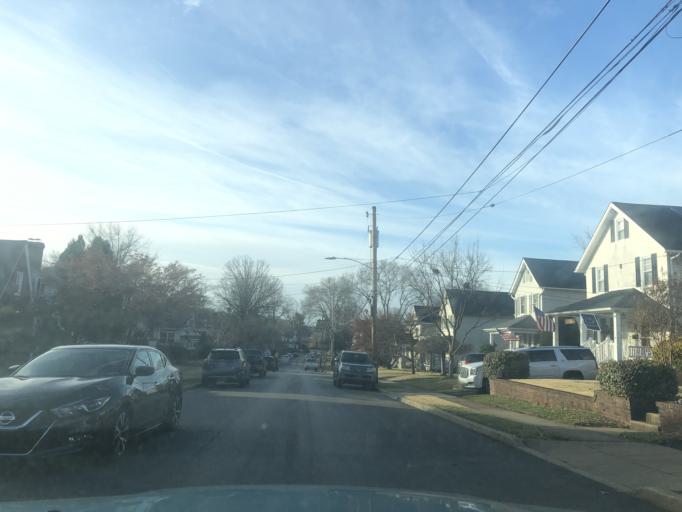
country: US
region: Pennsylvania
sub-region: Montgomery County
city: Glenside
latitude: 40.1123
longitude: -75.1519
